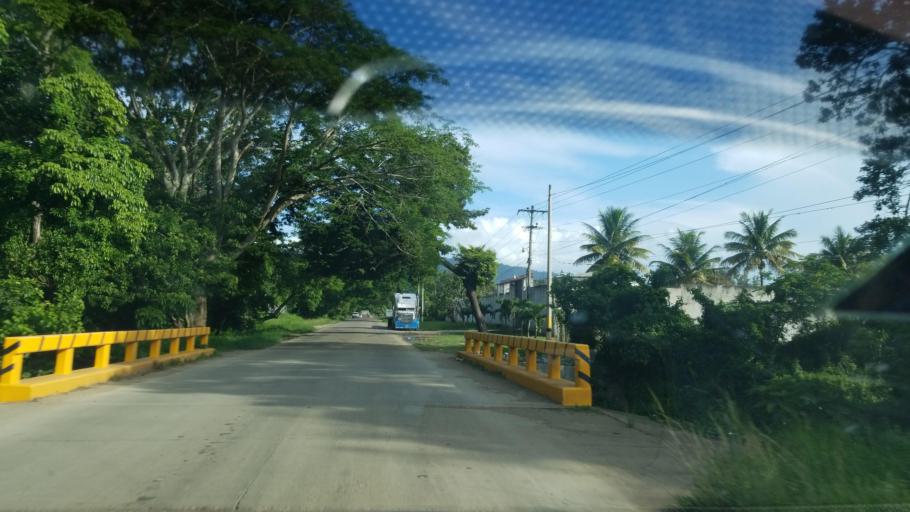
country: HN
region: El Paraiso
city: Cuyali
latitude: 13.8946
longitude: -86.5553
